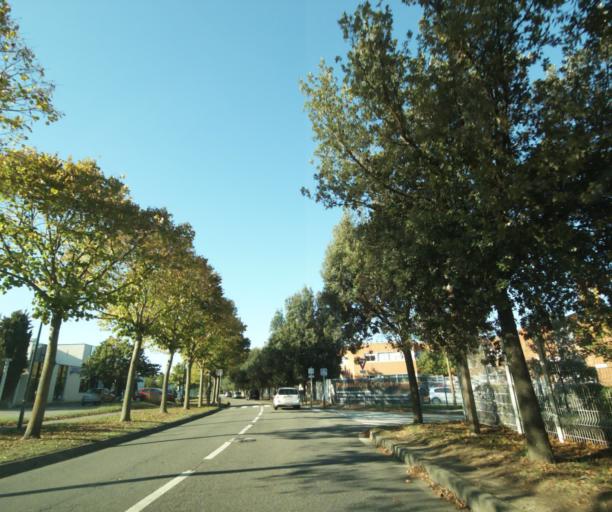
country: FR
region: Midi-Pyrenees
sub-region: Departement de la Haute-Garonne
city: Balma
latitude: 43.5825
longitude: 1.4938
